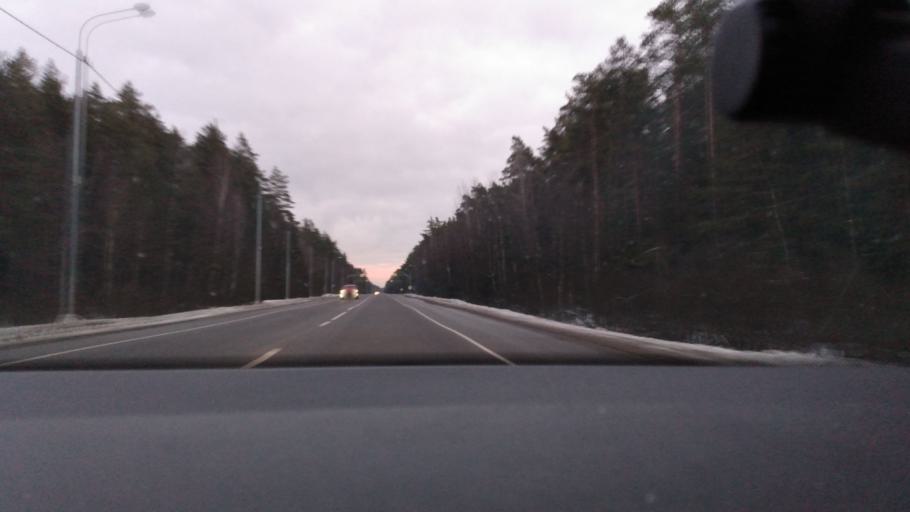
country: RU
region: Moskovskaya
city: Il'inskiy Pogost
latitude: 55.4607
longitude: 38.9831
